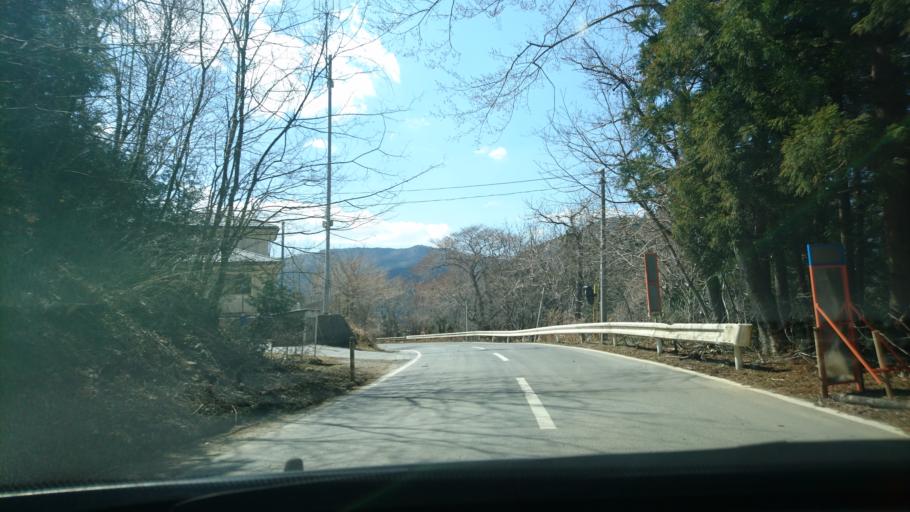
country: JP
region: Miyagi
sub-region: Oshika Gun
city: Onagawa Cho
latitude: 38.5165
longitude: 141.4731
